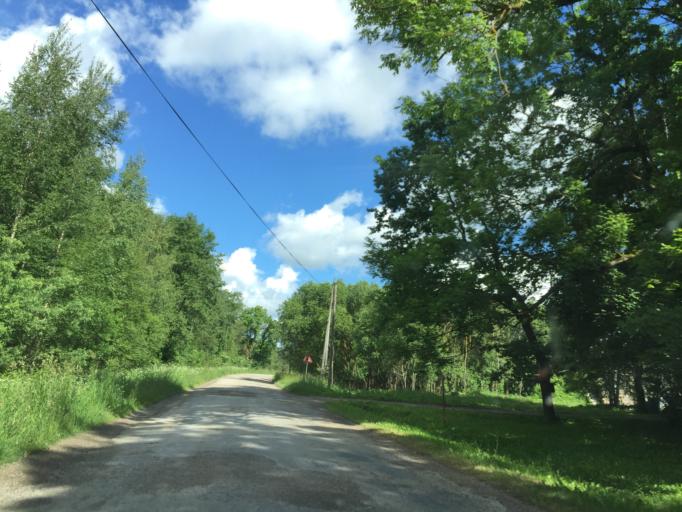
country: LV
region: Lecava
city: Iecava
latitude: 56.6109
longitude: 24.1902
